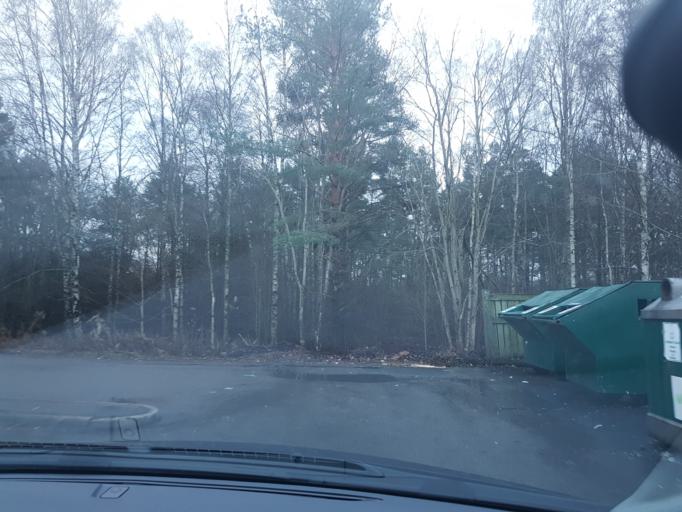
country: SE
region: Joenkoeping
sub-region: Vetlanda Kommun
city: Vetlanda
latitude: 57.4336
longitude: 15.0784
